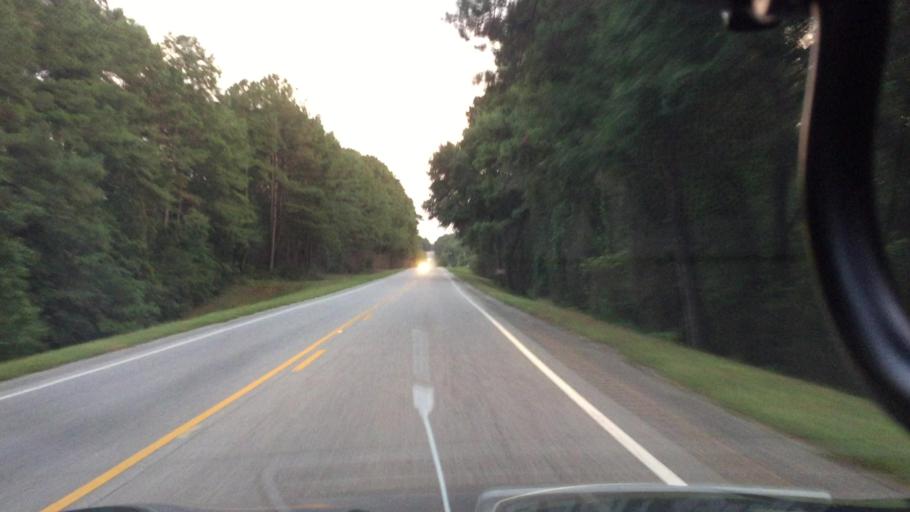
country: US
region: Alabama
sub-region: Coffee County
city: New Brockton
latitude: 31.3910
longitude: -85.8772
